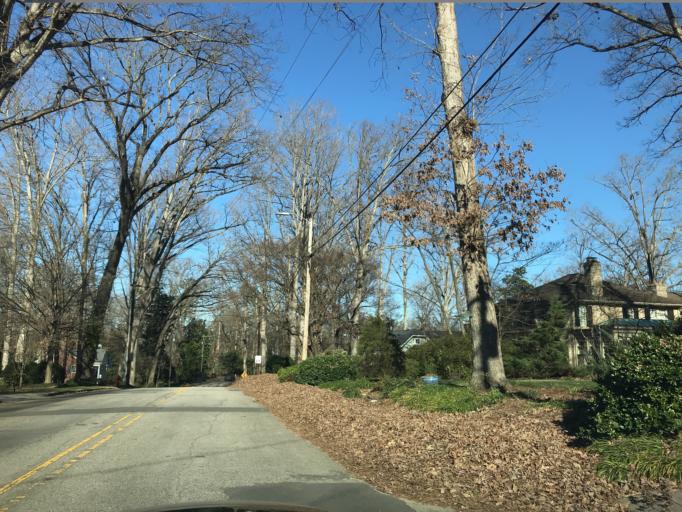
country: US
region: North Carolina
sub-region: Wake County
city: West Raleigh
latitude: 35.8169
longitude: -78.6437
